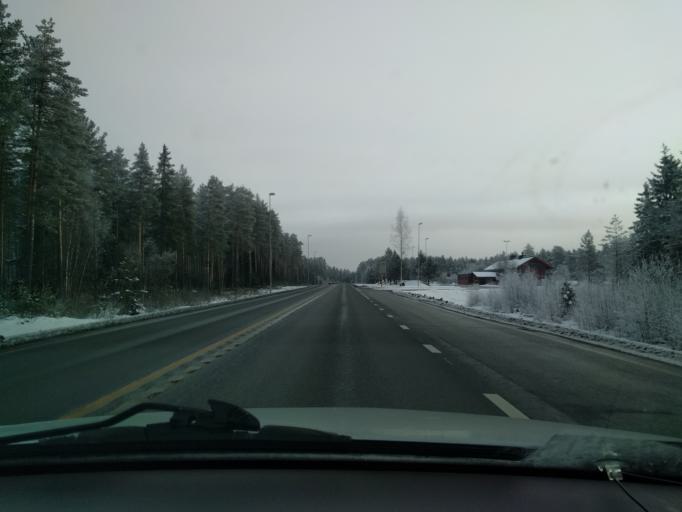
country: NO
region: Hedmark
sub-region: Loten
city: Loten
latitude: 60.8582
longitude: 11.3968
